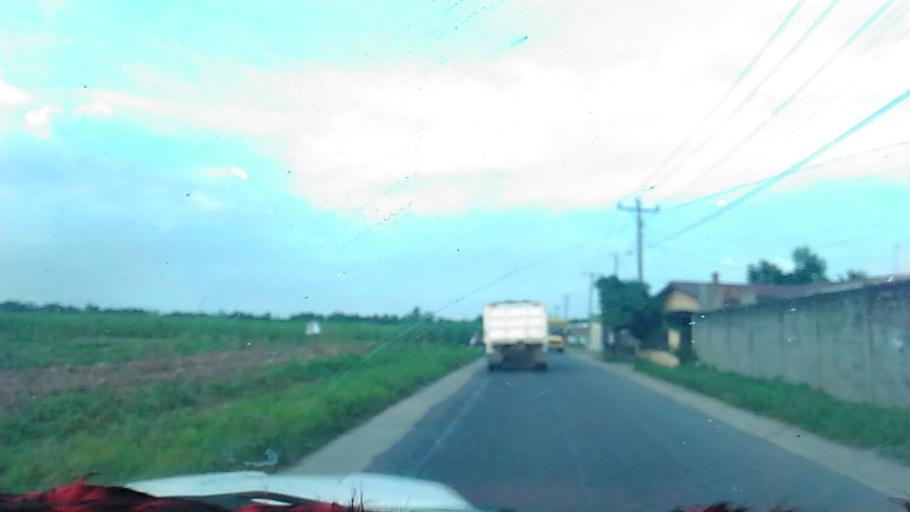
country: ID
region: North Sumatra
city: Labuhan Deli
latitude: 3.7036
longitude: 98.5704
